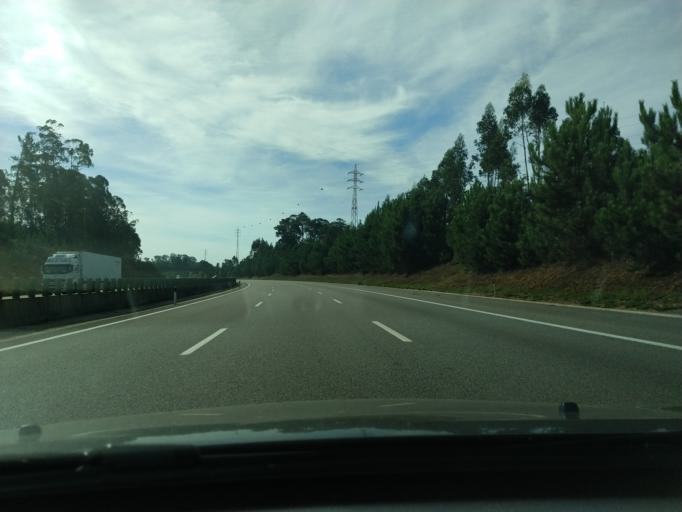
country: PT
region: Aveiro
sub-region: Ovar
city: Valega
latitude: 40.8490
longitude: -8.5575
